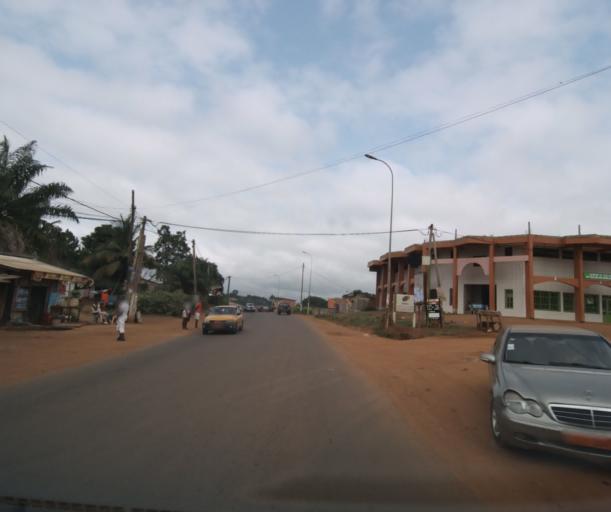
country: CM
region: Centre
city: Yaounde
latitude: 3.8010
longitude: 11.5243
